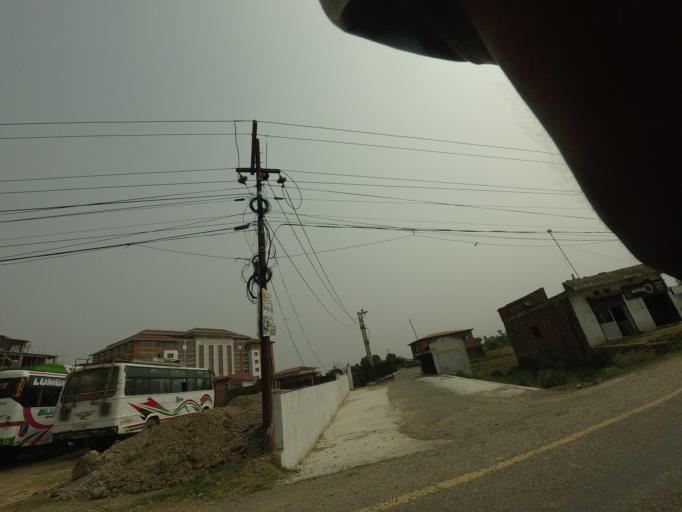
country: IN
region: Uttar Pradesh
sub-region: Maharajganj
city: Nautanwa
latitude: 27.4913
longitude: 83.3013
